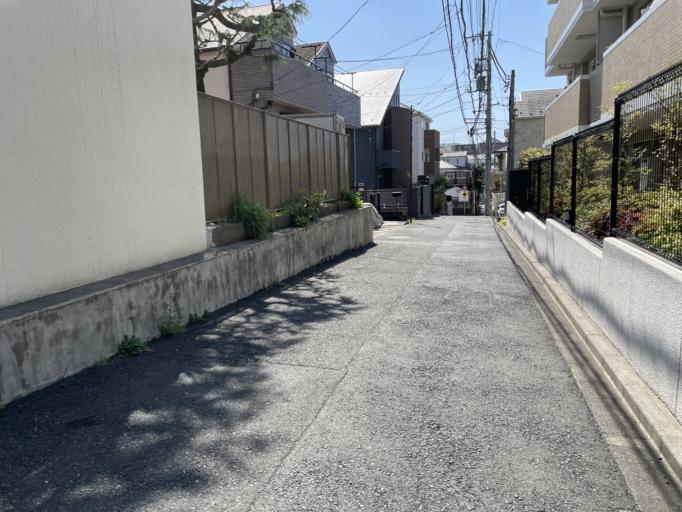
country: JP
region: Tokyo
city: Tokyo
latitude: 35.7077
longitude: 139.6747
